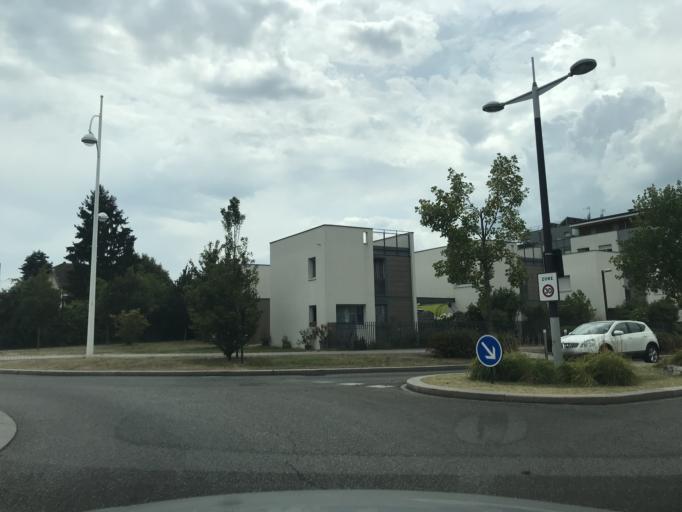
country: FR
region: Rhone-Alpes
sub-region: Departement de la Savoie
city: Brison-Saint-Innocent
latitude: 45.7002
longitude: 5.8921
